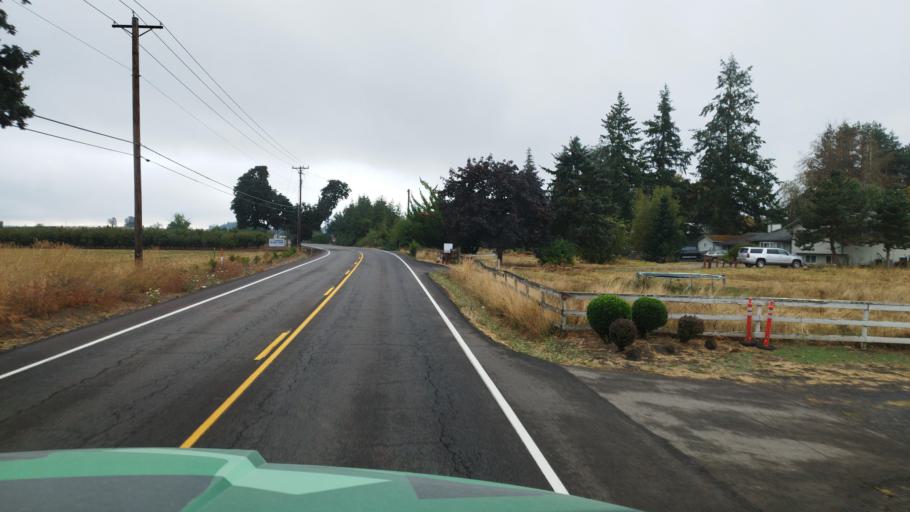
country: US
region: Oregon
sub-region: Yamhill County
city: Yamhill
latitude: 45.3324
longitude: -123.1848
